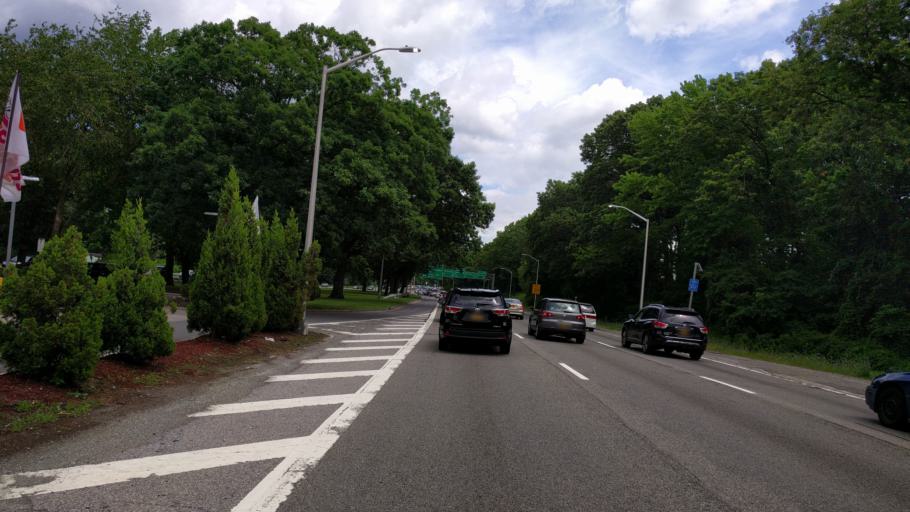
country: US
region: New York
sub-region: Nassau County
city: Bellerose Terrace
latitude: 40.7249
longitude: -73.7717
